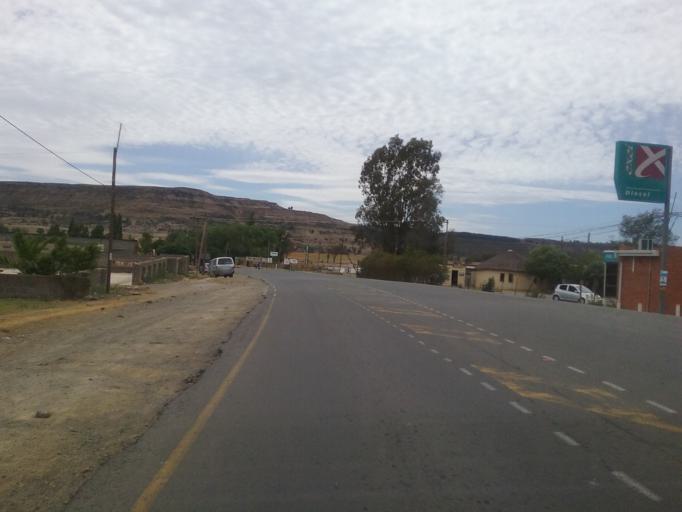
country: LS
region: Maseru
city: Nako
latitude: -29.6229
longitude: 27.4957
